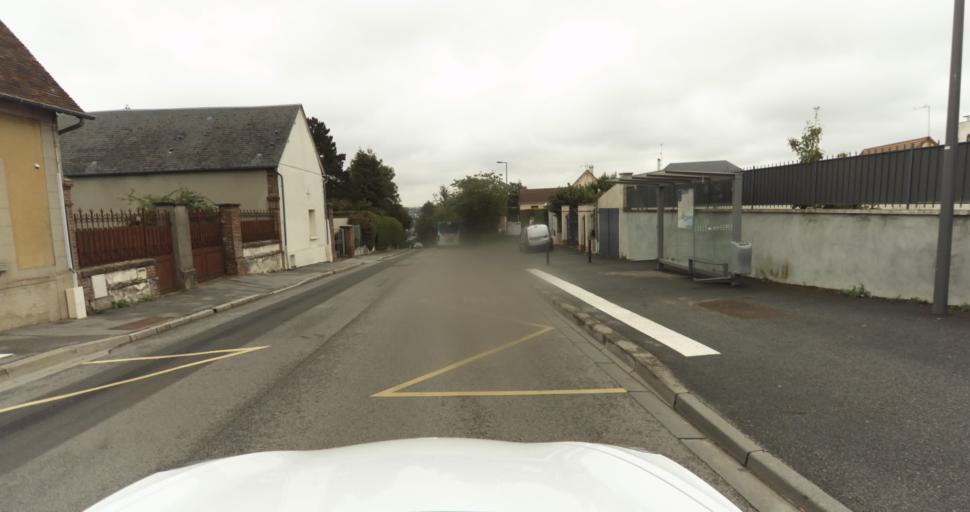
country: FR
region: Haute-Normandie
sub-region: Departement de l'Eure
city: Evreux
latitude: 49.0289
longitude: 1.1360
